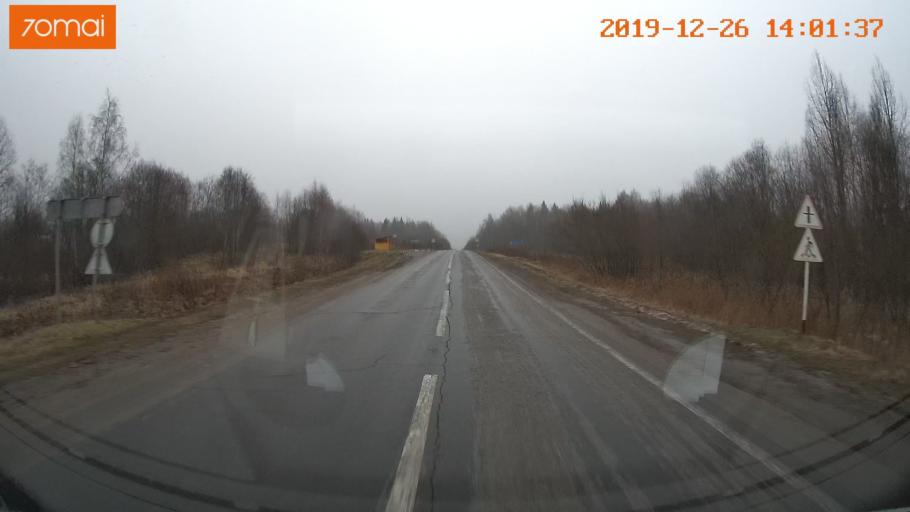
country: RU
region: Jaroslavl
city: Poshekhon'ye
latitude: 58.5492
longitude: 38.7672
